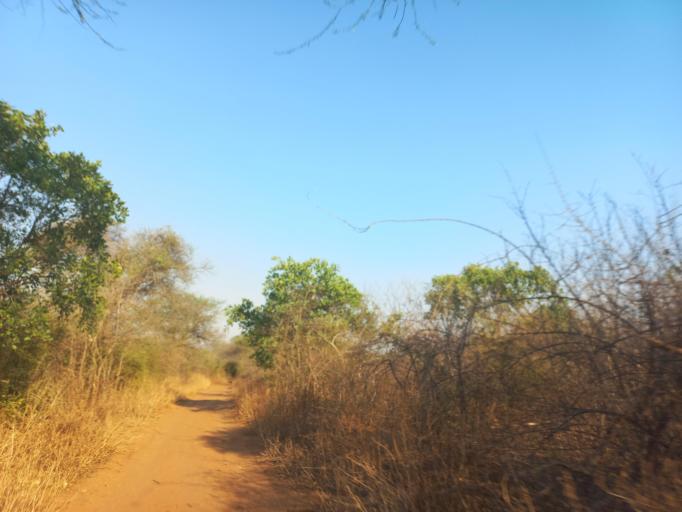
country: ZM
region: Lusaka
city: Luangwa
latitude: -15.4208
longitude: 30.2714
